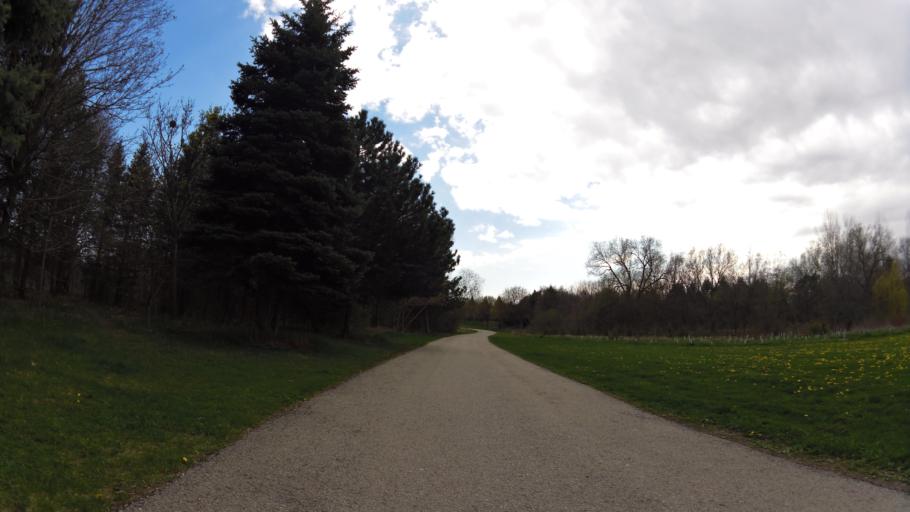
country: CA
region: Ontario
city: Etobicoke
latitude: 43.6331
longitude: -79.5861
